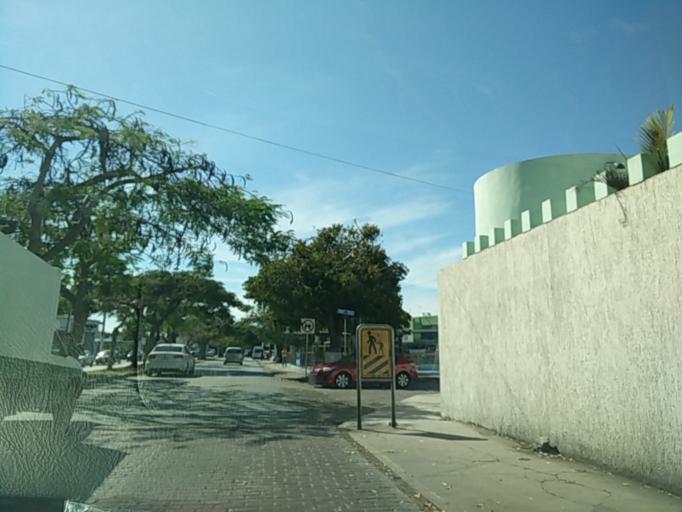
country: MX
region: Yucatan
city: Merida
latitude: 20.9892
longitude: -89.6082
